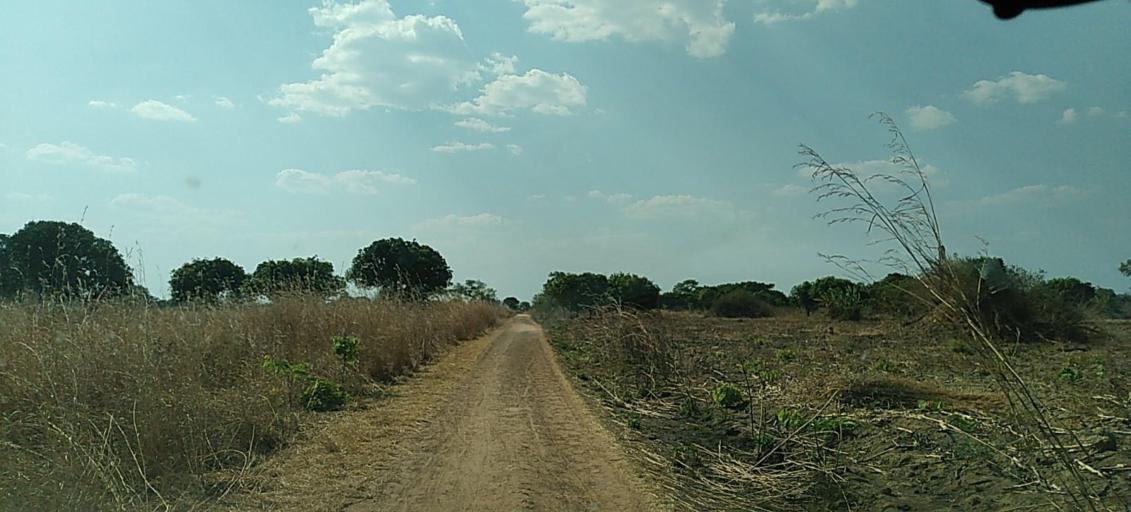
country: ZM
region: North-Western
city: Kalengwa
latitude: -13.0955
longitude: 24.9781
